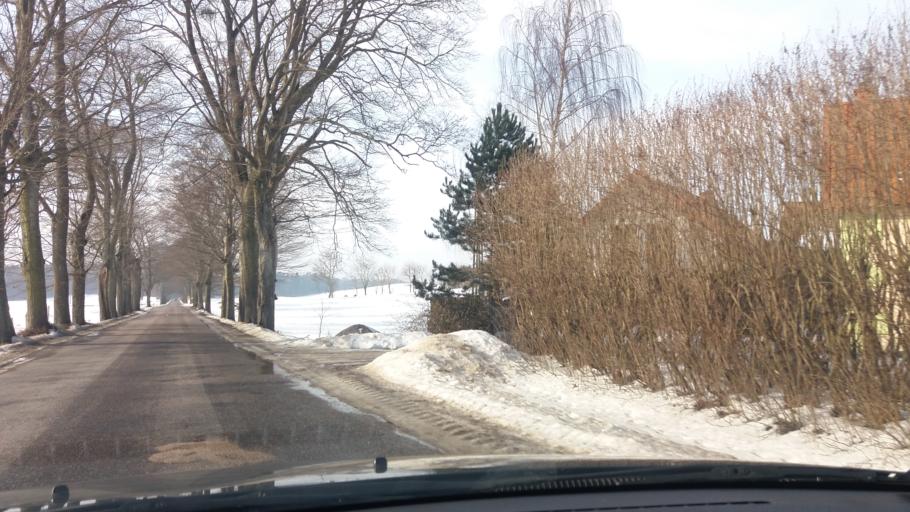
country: PL
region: Warmian-Masurian Voivodeship
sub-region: Powiat lidzbarski
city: Lidzbark Warminski
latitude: 54.1072
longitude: 20.6536
